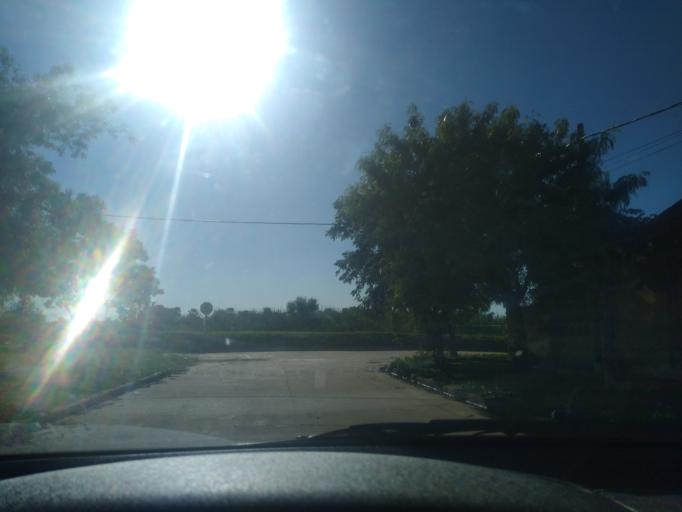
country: AR
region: Chaco
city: Puerto Vilelas
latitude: -27.5175
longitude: -58.9460
